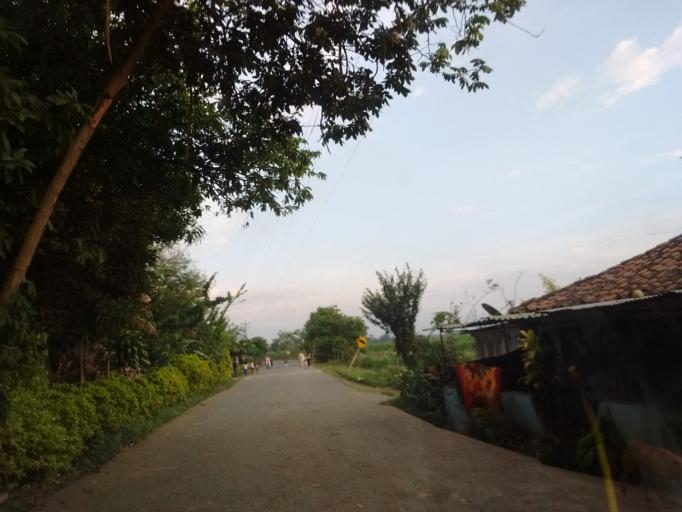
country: CO
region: Cauca
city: Puerto Tejada
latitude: 3.2151
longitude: -76.4450
